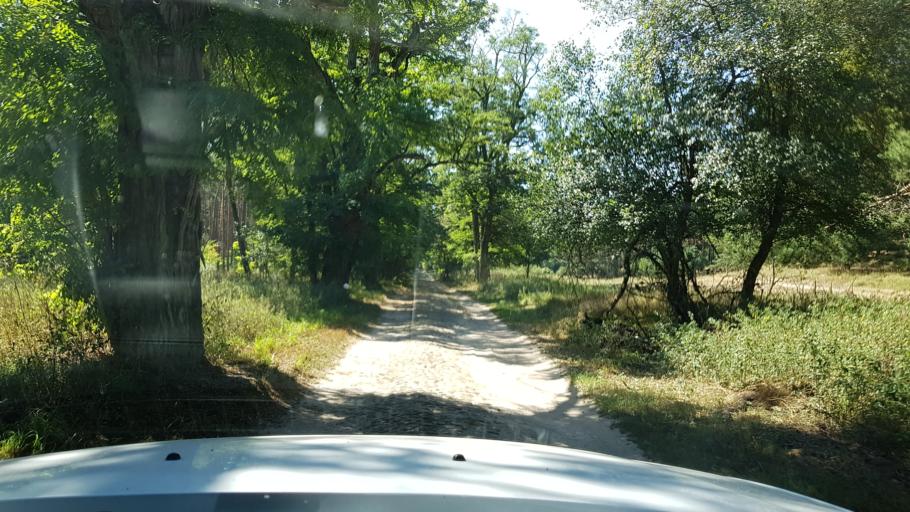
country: PL
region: West Pomeranian Voivodeship
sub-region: Powiat gryfinski
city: Cedynia
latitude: 52.8482
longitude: 14.2409
